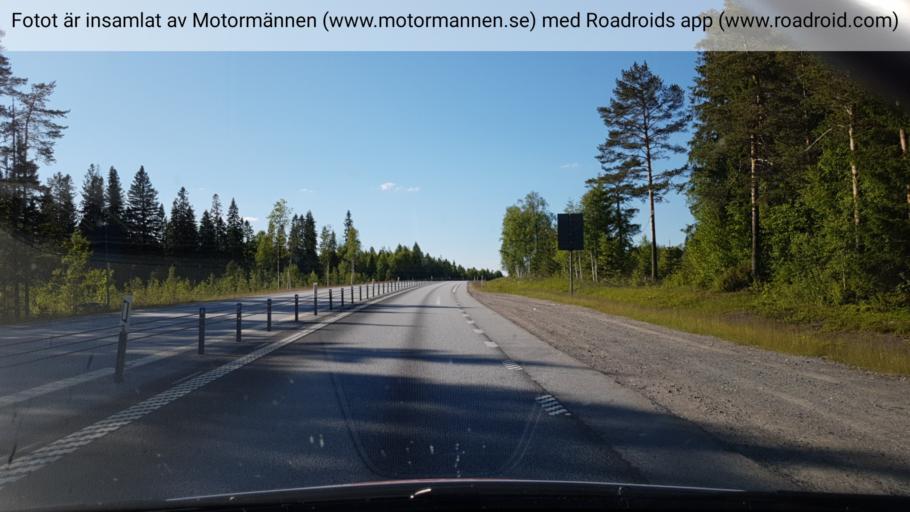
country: SE
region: Vaesterbotten
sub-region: Vannas Kommun
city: Vannasby
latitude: 63.9029
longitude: 19.8959
